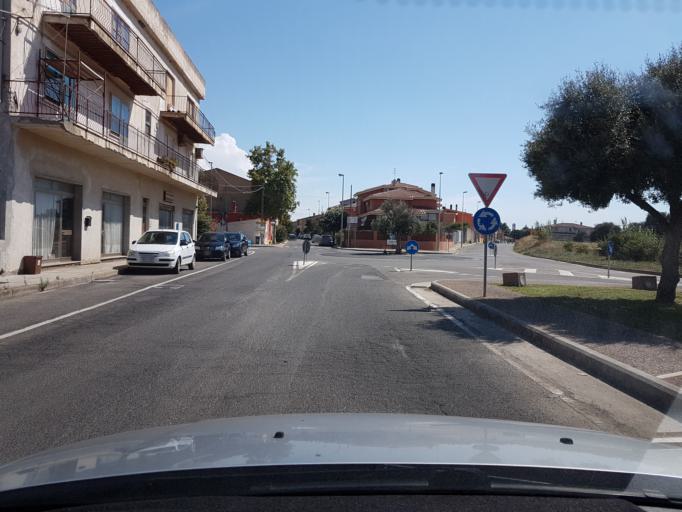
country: IT
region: Sardinia
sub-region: Provincia di Oristano
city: Cabras
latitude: 39.9374
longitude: 8.5315
